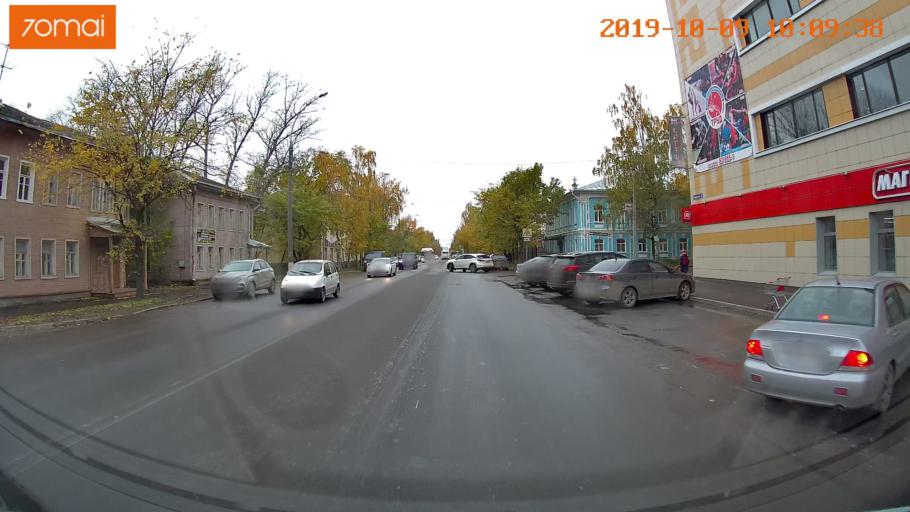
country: RU
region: Vologda
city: Vologda
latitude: 59.2129
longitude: 39.9025
